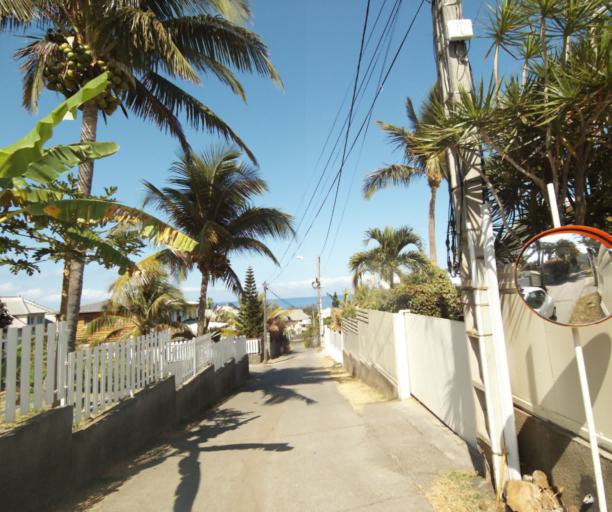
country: RE
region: Reunion
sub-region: Reunion
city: Trois-Bassins
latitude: -21.1047
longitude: 55.2510
